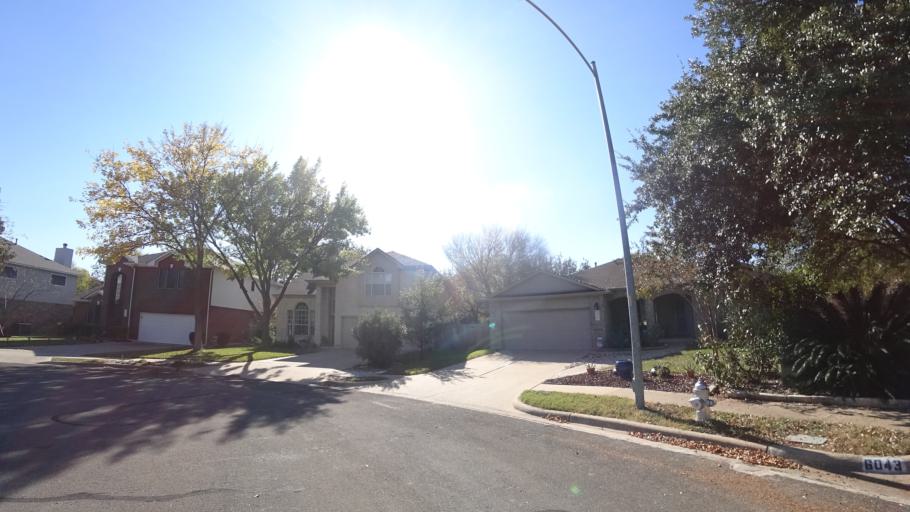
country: US
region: Texas
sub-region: Travis County
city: Barton Creek
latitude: 30.2277
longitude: -97.8643
